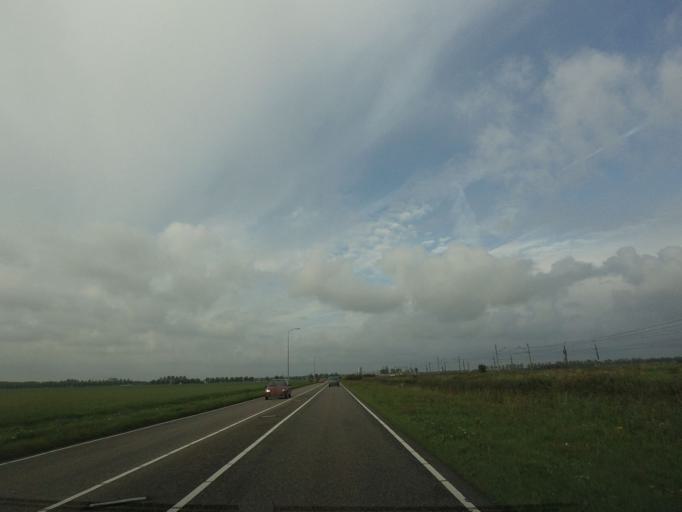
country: NL
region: North Holland
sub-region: Gemeente Haarlemmermeer
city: Hoofddorp
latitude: 52.2727
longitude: 4.6643
